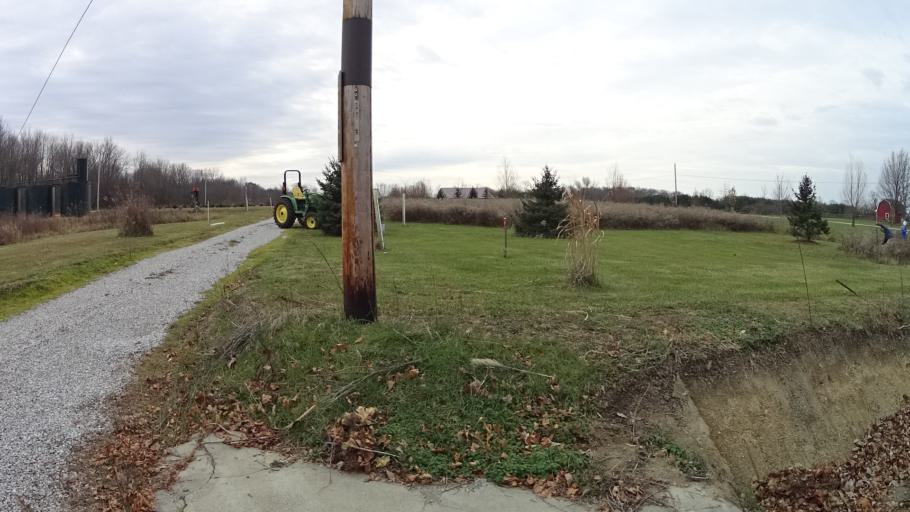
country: US
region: Ohio
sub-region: Medina County
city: Lodi
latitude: 41.1364
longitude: -82.0637
